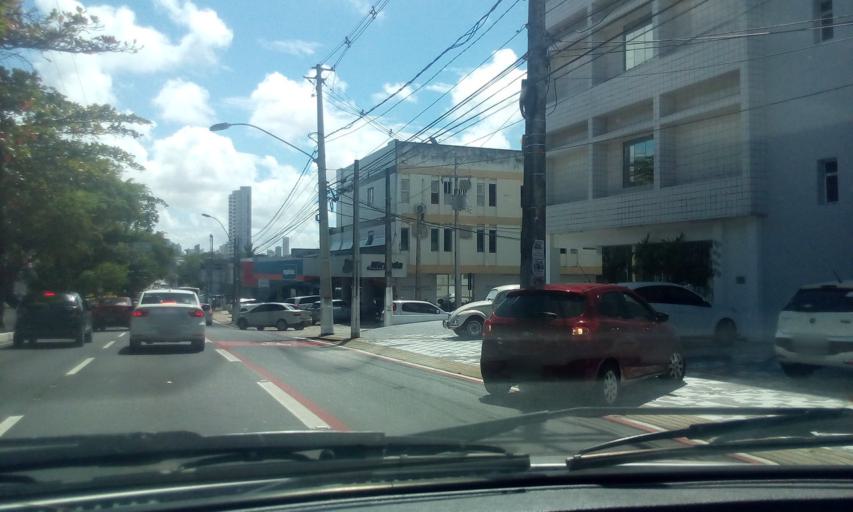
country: BR
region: Rio Grande do Norte
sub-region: Natal
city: Natal
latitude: -5.8012
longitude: -35.2064
